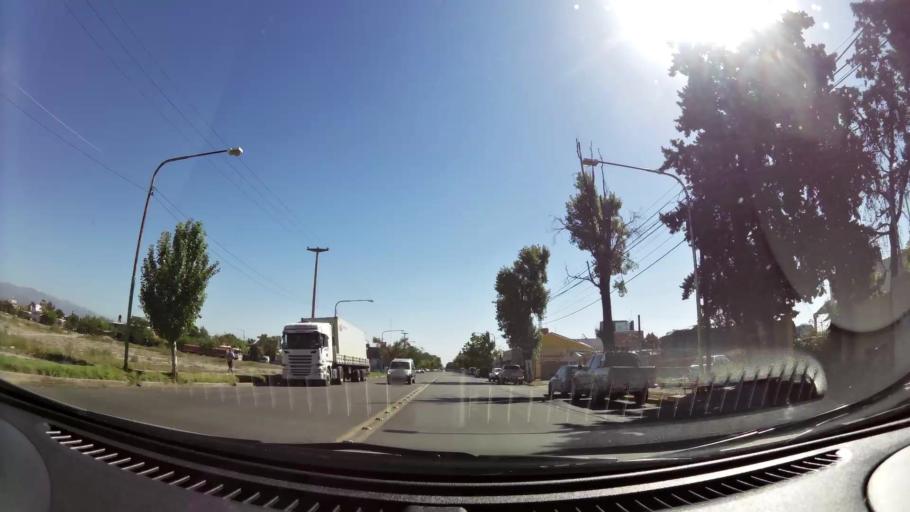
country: AR
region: Mendoza
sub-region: Departamento de Maipu
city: Maipu
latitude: -32.9651
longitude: -68.7913
